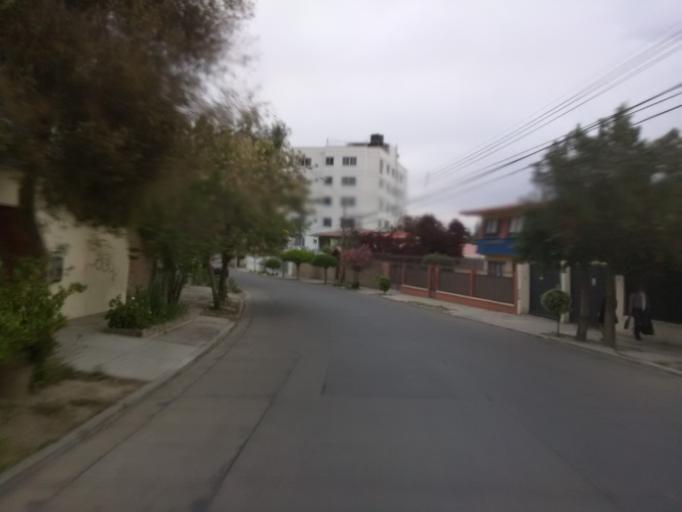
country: BO
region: Cochabamba
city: Cochabamba
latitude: -17.3743
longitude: -66.1630
